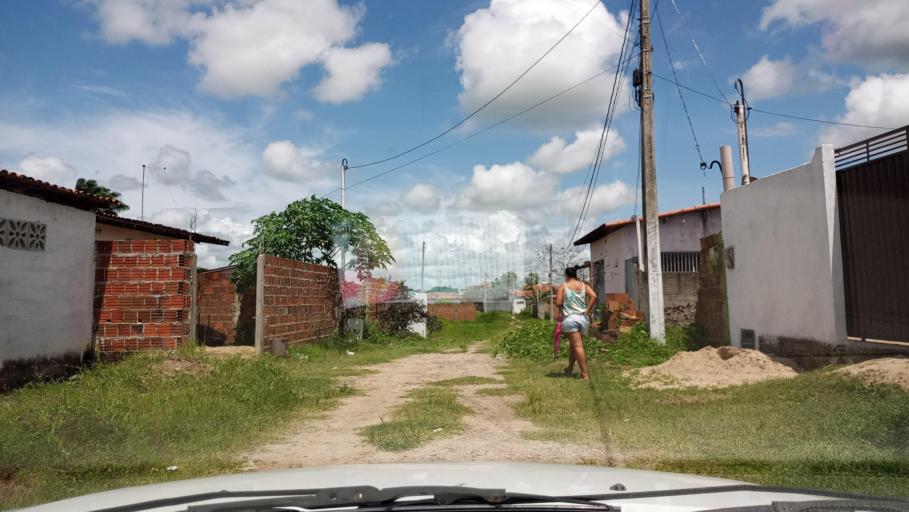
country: BR
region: Rio Grande do Norte
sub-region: Goianinha
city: Goianinha
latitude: -6.2571
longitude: -35.2057
